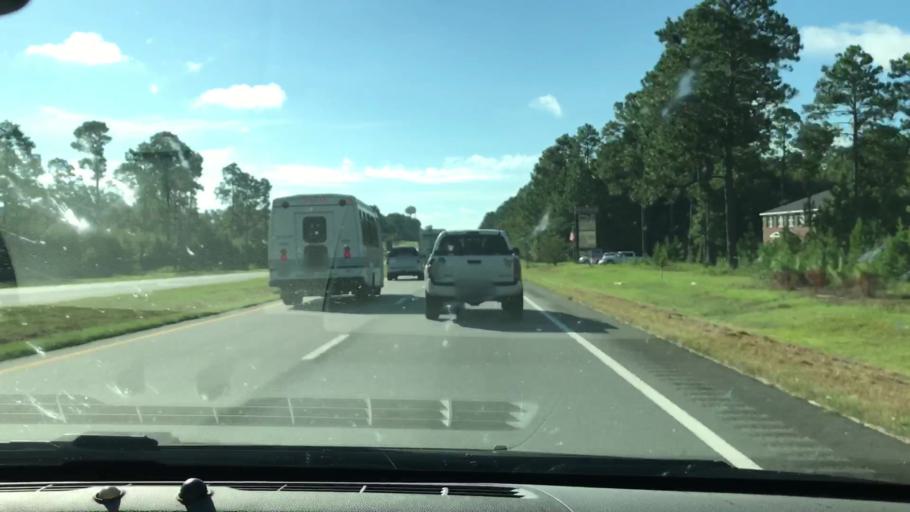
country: US
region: Georgia
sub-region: Lee County
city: Leesburg
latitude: 31.6466
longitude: -84.2595
